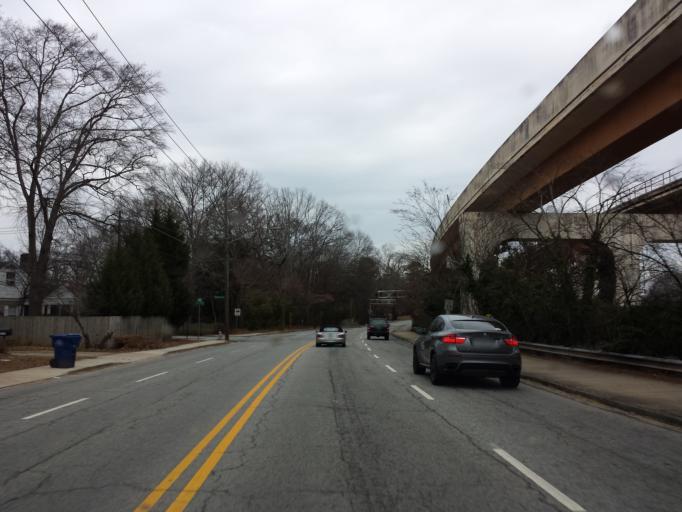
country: US
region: Georgia
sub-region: DeKalb County
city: Decatur
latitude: 33.7643
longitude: -84.3174
